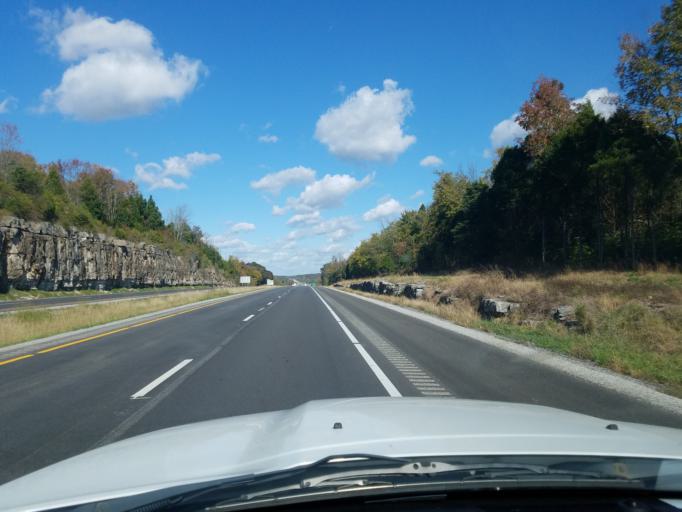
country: US
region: Kentucky
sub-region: Warren County
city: Bowling Green
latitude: 36.9674
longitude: -86.4989
